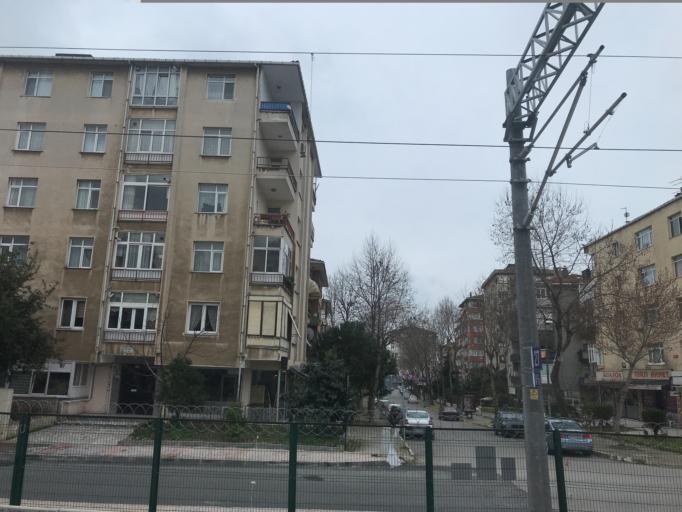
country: TR
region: Istanbul
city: Maltepe
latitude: 40.8970
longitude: 29.1711
